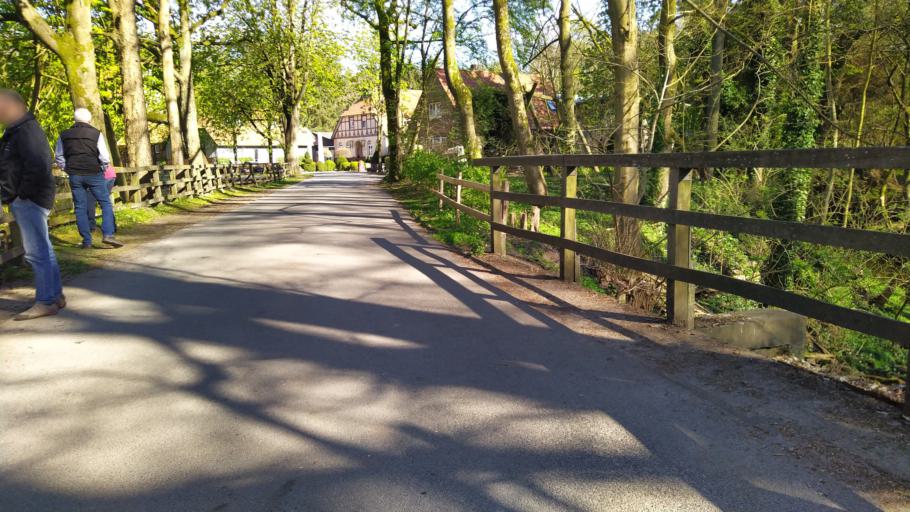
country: DE
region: Lower Saxony
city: Klein Meckelsen
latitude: 53.2950
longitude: 9.4368
